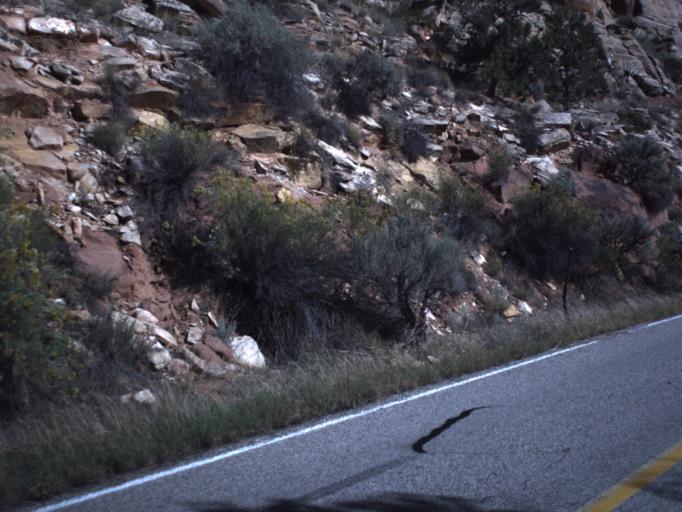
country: US
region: Utah
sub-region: San Juan County
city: Monticello
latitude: 38.0105
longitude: -109.5384
